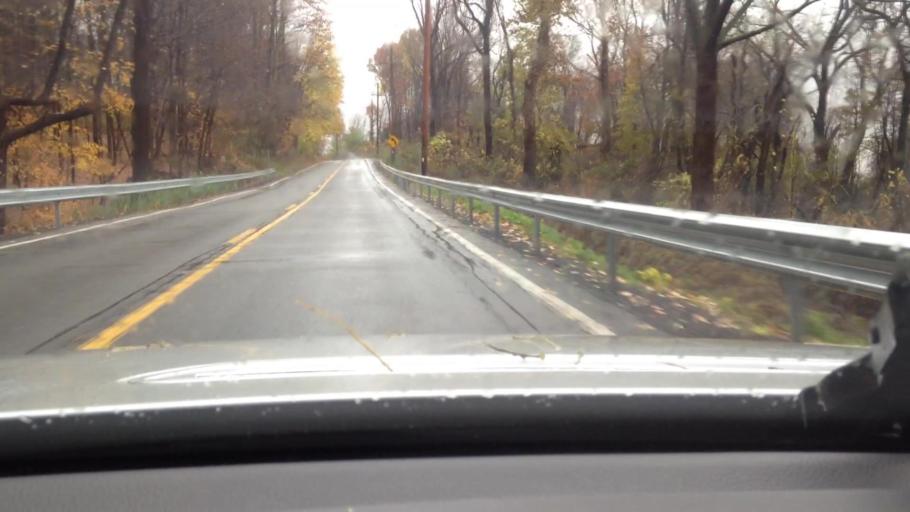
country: US
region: New York
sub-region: Orange County
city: Cornwall-on-Hudson
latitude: 41.4534
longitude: -73.9824
